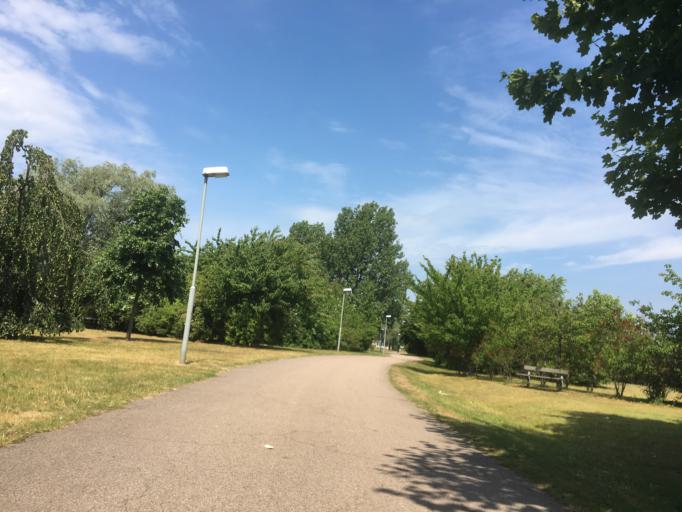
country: SE
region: Skane
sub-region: Landskrona
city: Landskrona
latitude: 55.8897
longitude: 12.8146
